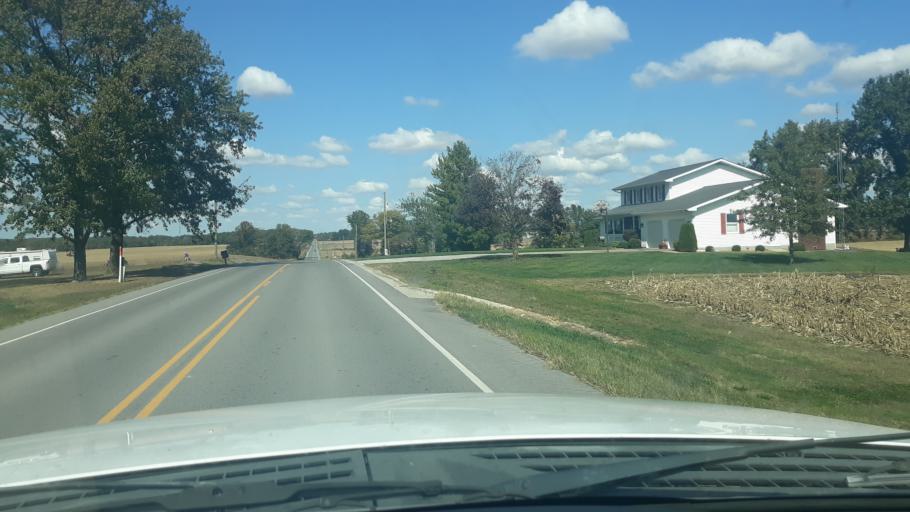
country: US
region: Illinois
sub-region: Saline County
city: Eldorado
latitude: 37.7946
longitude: -88.4848
